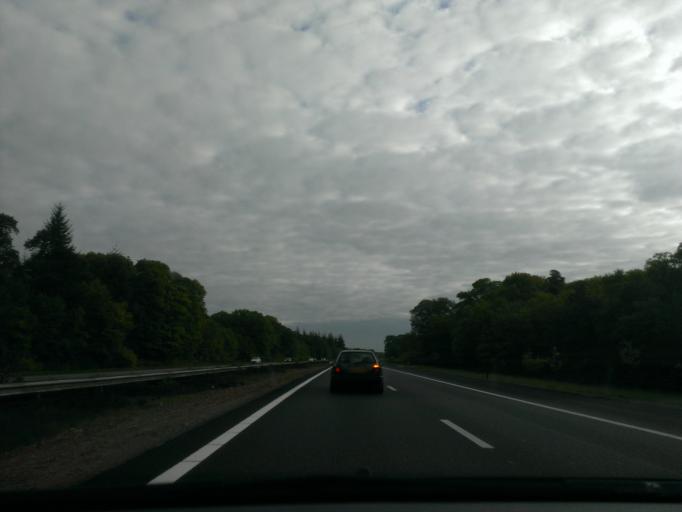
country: NL
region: Gelderland
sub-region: Gemeente Heerde
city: Heerde
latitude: 52.4367
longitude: 6.0199
